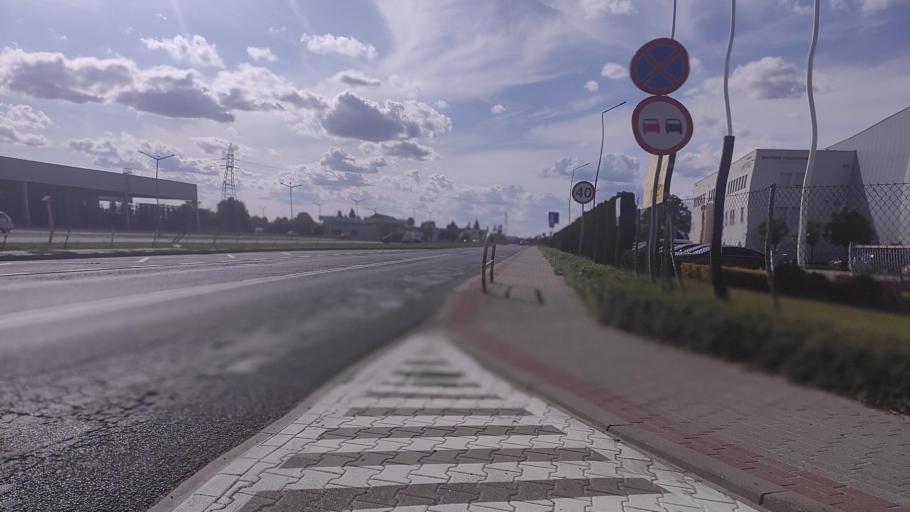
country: PL
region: Greater Poland Voivodeship
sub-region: Powiat poznanski
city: Swarzedz
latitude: 52.3985
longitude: 17.1066
